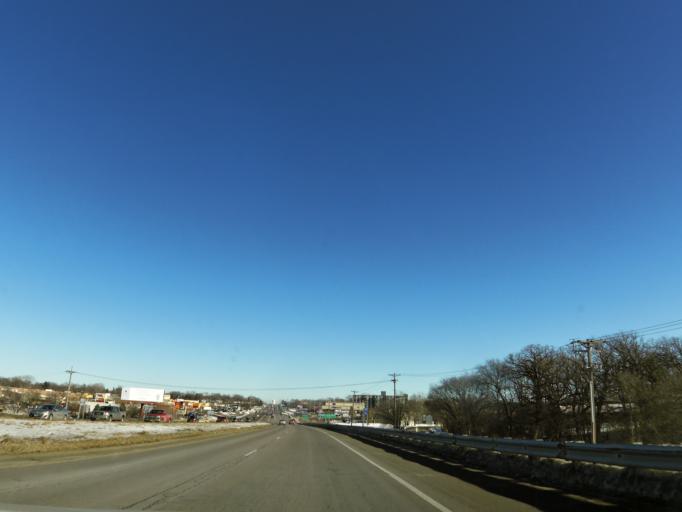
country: US
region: Minnesota
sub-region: Hennepin County
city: Saint Louis Park
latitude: 44.9345
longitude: -93.3940
